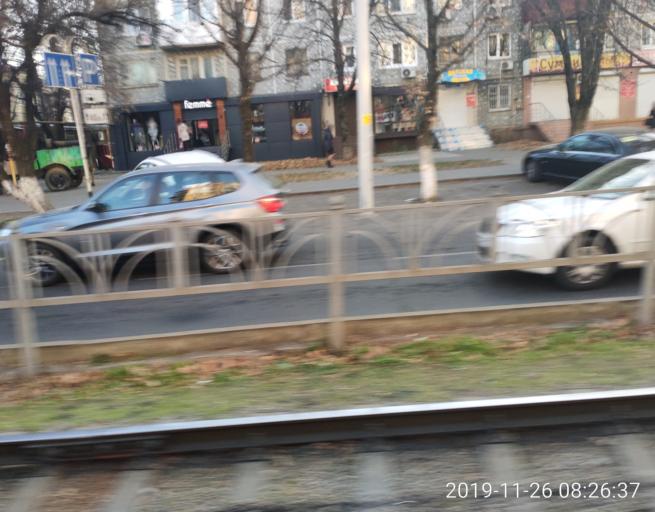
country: RU
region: Krasnodarskiy
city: Krasnodar
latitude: 45.0619
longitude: 39.0019
